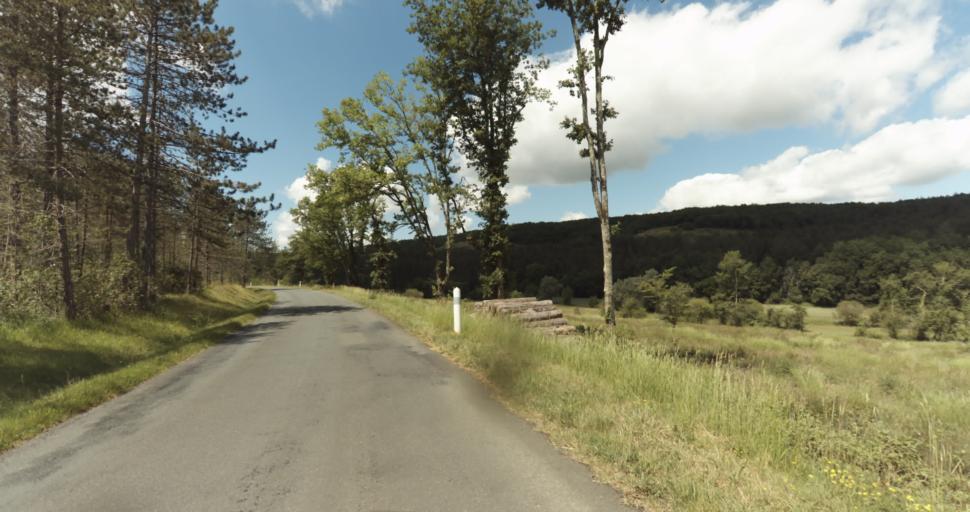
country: FR
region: Aquitaine
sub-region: Departement de la Dordogne
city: Beaumont-du-Perigord
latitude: 44.7662
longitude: 0.7446
